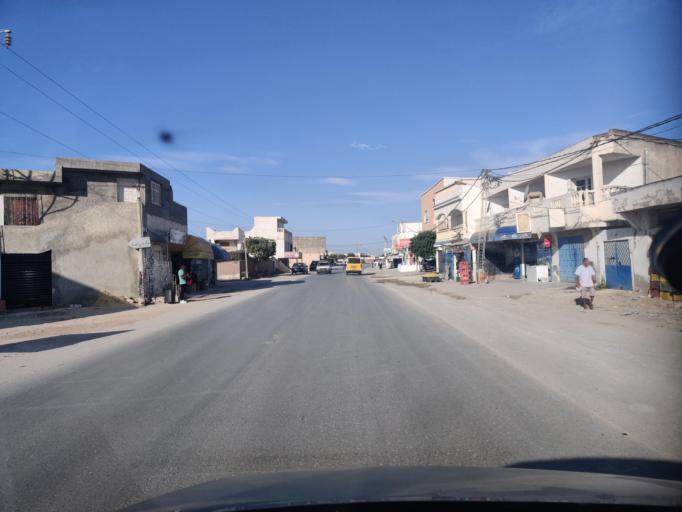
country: TN
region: Ariana
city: Ariana
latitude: 36.9562
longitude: 10.2138
